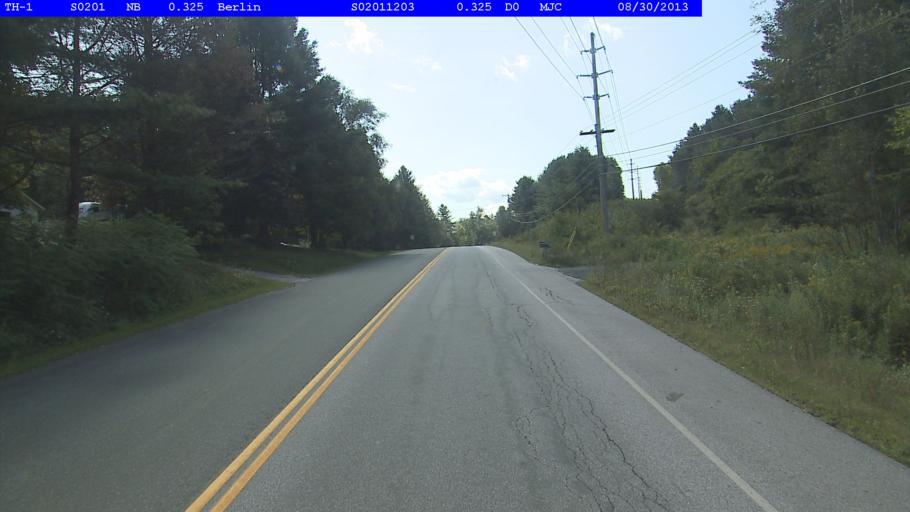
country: US
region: Vermont
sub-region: Washington County
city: Montpelier
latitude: 44.2334
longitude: -72.5632
